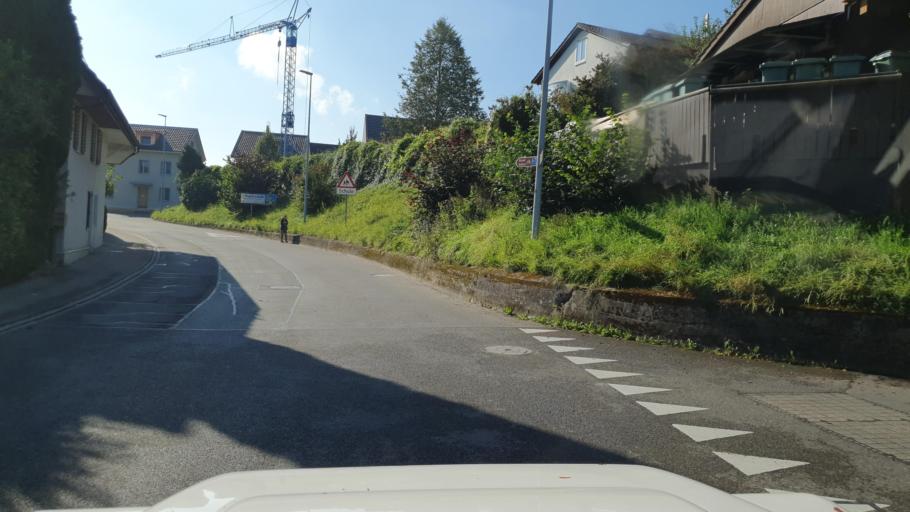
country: CH
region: Aargau
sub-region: Bezirk Bremgarten
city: Sarmenstorf
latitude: 47.3163
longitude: 8.2744
